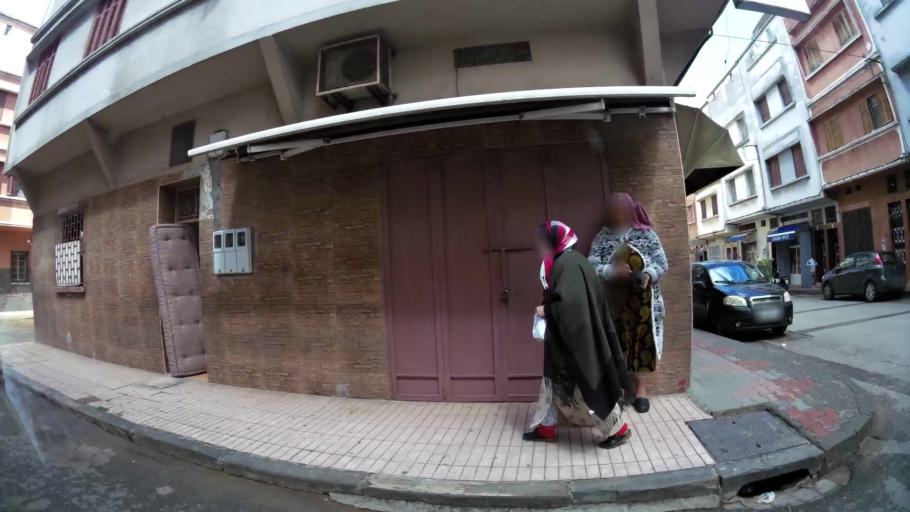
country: MA
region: Grand Casablanca
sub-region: Casablanca
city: Casablanca
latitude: 33.5603
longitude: -7.6062
